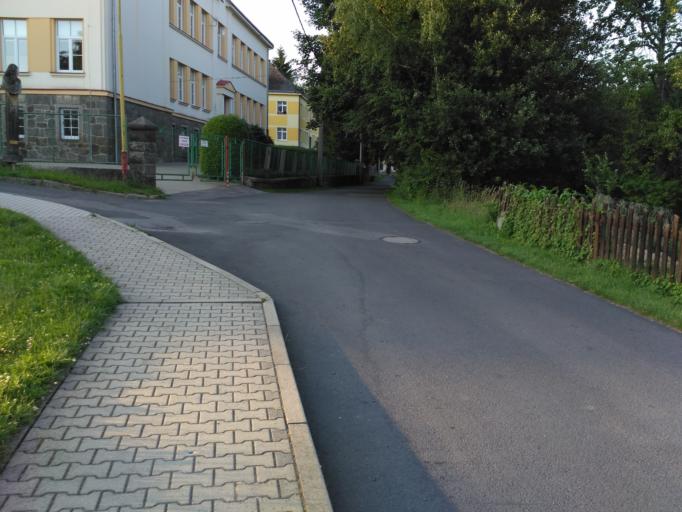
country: CZ
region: Ustecky
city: Dolni Poustevna
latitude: 50.9834
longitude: 14.2870
